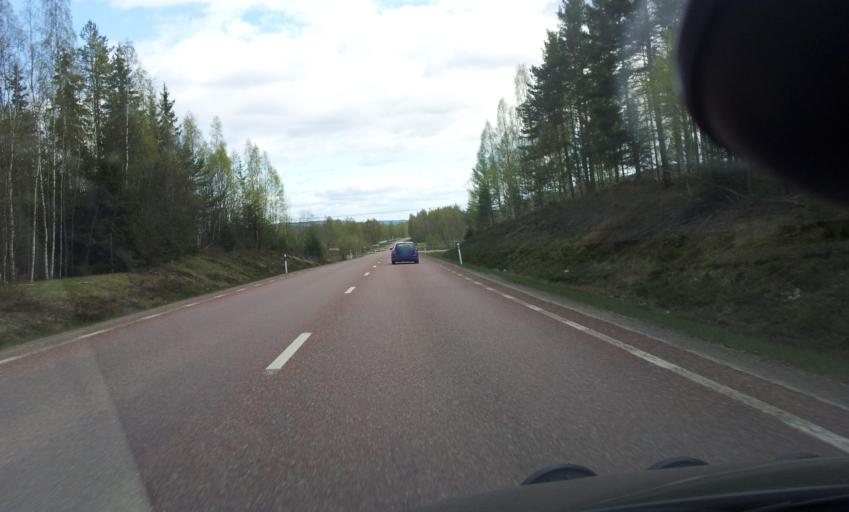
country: SE
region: Gaevleborg
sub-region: Ljusdals Kommun
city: Jaervsoe
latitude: 61.7689
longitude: 16.1562
